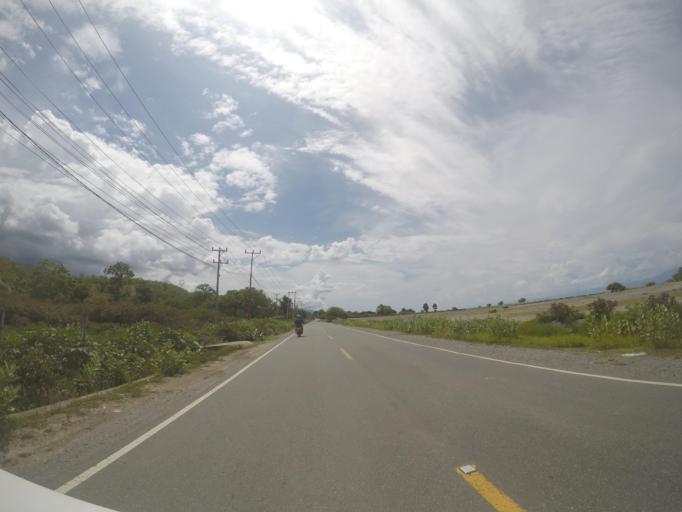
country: TL
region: Liquica
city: Liquica
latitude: -8.5780
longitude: 125.3667
